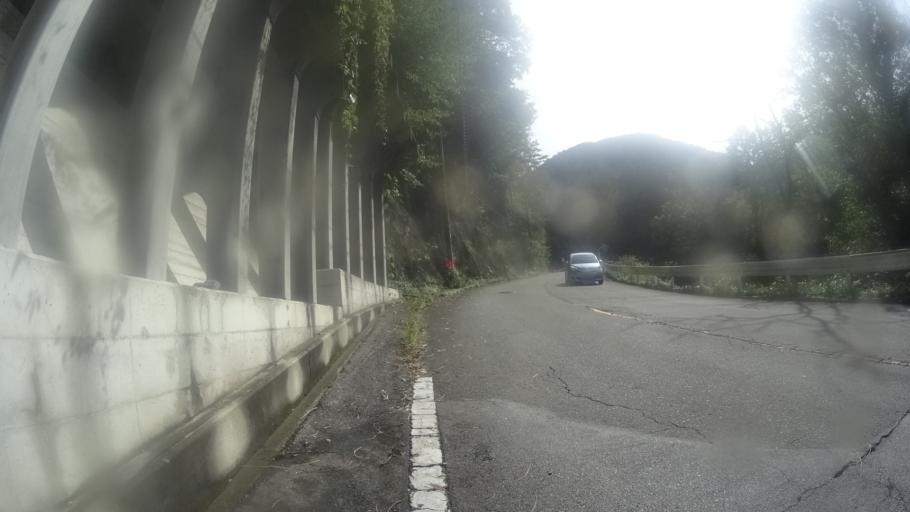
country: JP
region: Yamanashi
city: Otsuki
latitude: 35.7886
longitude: 138.9272
